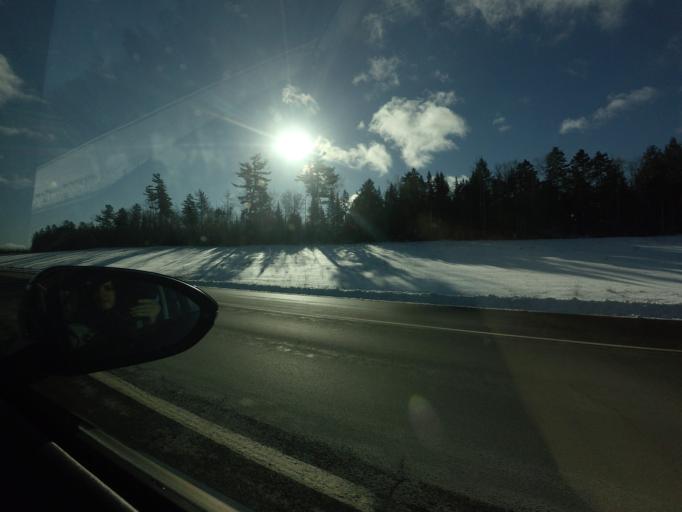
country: CA
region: New Brunswick
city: Fredericton
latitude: 45.8756
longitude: -66.6281
